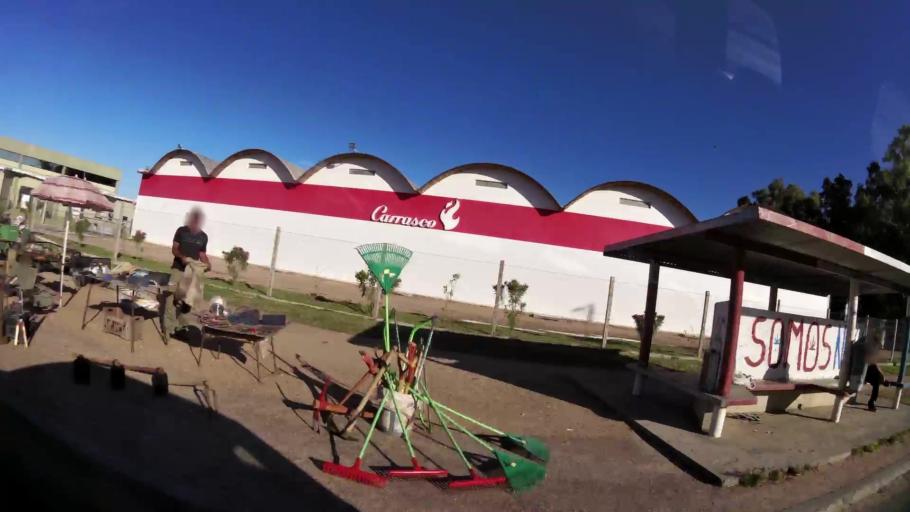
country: UY
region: Canelones
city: Paso de Carrasco
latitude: -34.8650
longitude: -56.0580
